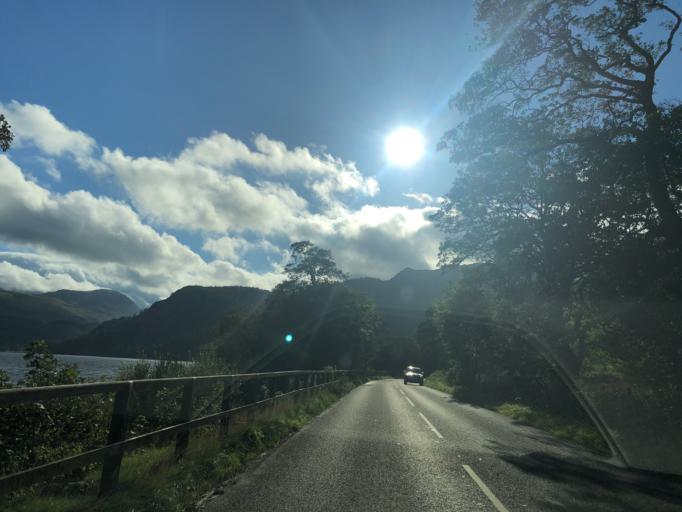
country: GB
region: England
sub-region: Cumbria
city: Ambleside
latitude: 54.5662
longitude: -2.9393
